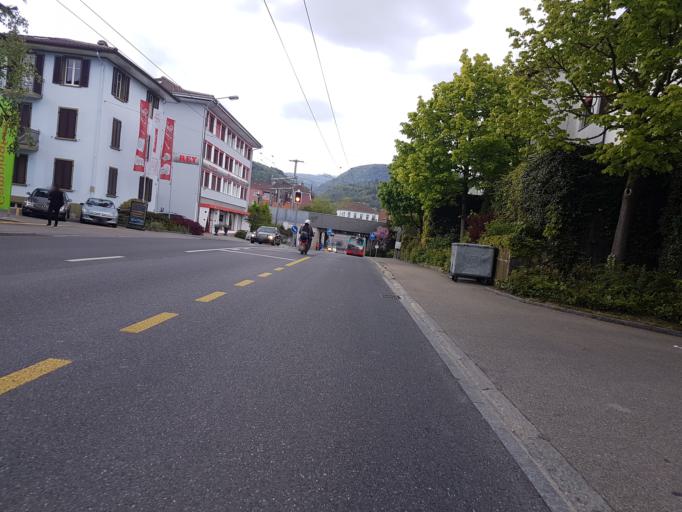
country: CH
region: Bern
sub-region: Biel/Bienne District
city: Brugg
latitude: 47.1446
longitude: 7.2743
